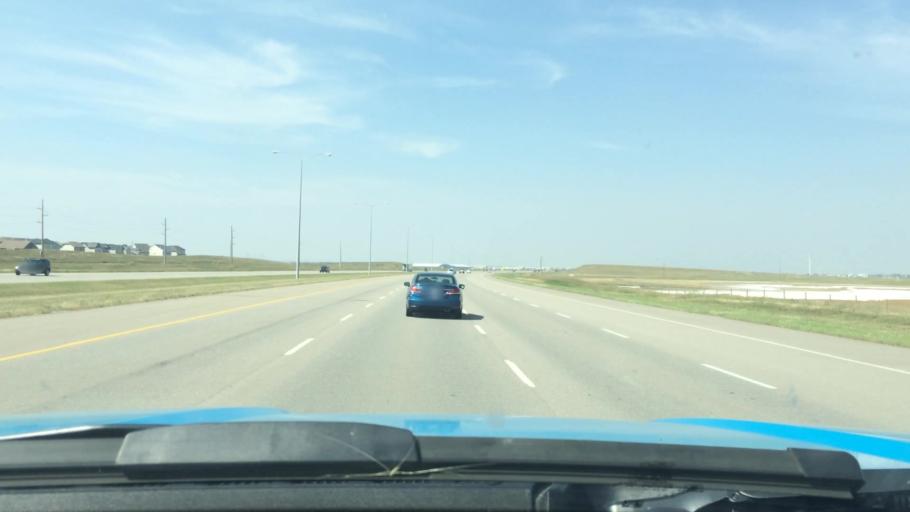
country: CA
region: Alberta
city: Chestermere
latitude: 50.9203
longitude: -113.9147
